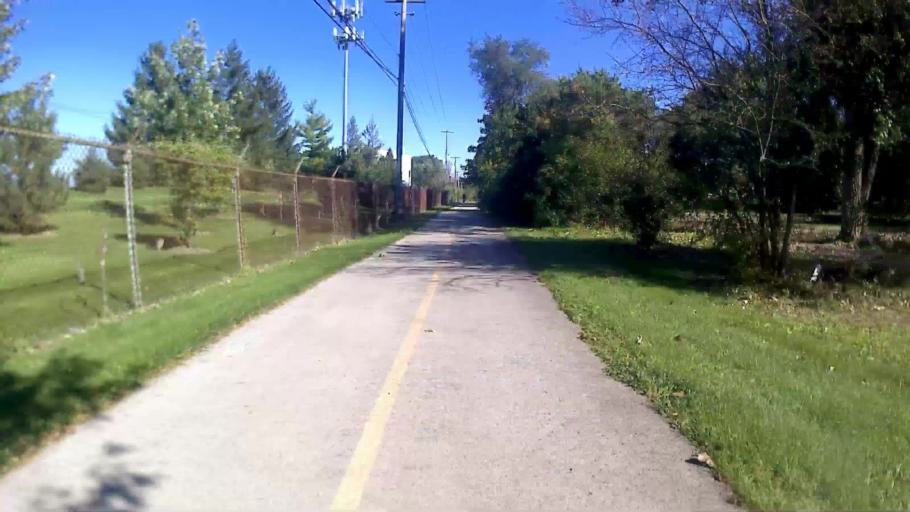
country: US
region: Illinois
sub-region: DuPage County
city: Addison
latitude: 41.9383
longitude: -87.9881
